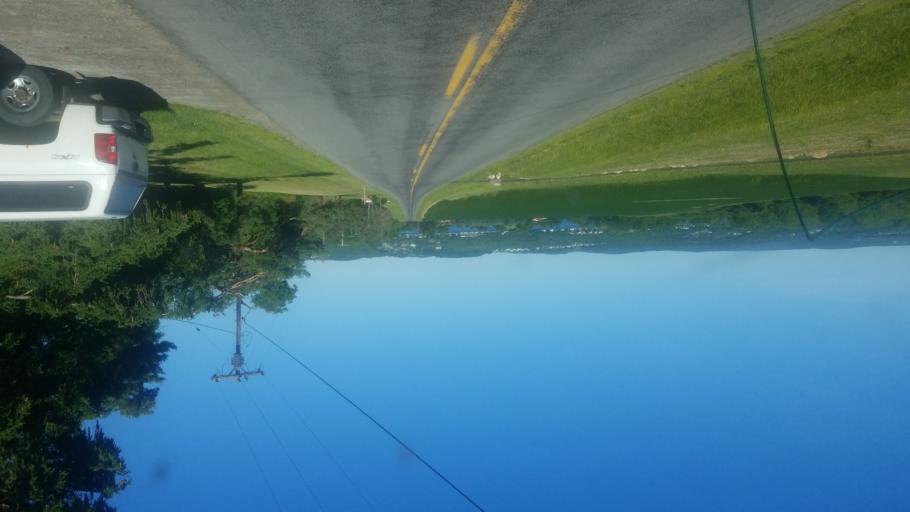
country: US
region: New York
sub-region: Ontario County
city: Canandaigua
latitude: 42.8397
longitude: -77.2457
